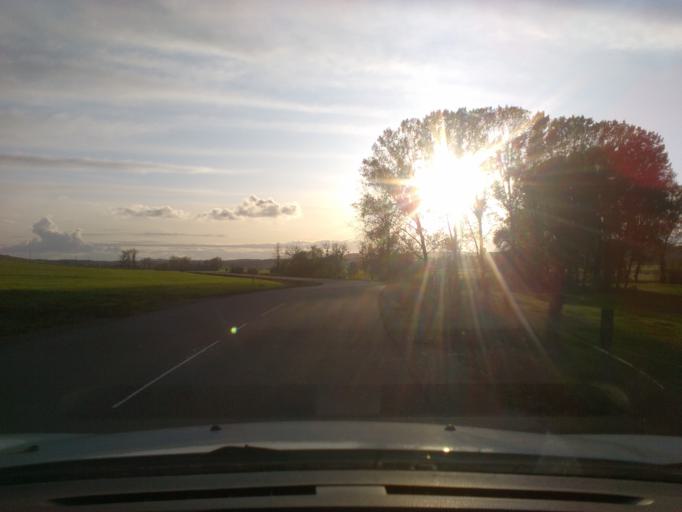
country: FR
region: Lorraine
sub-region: Departement des Vosges
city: Mirecourt
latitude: 48.2590
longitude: 6.1600
